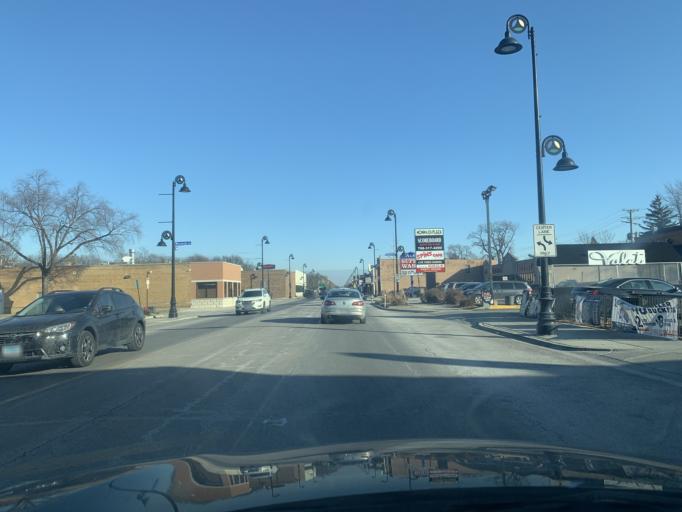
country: US
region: Illinois
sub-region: Cook County
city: Berwyn
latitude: 41.8650
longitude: -87.8023
